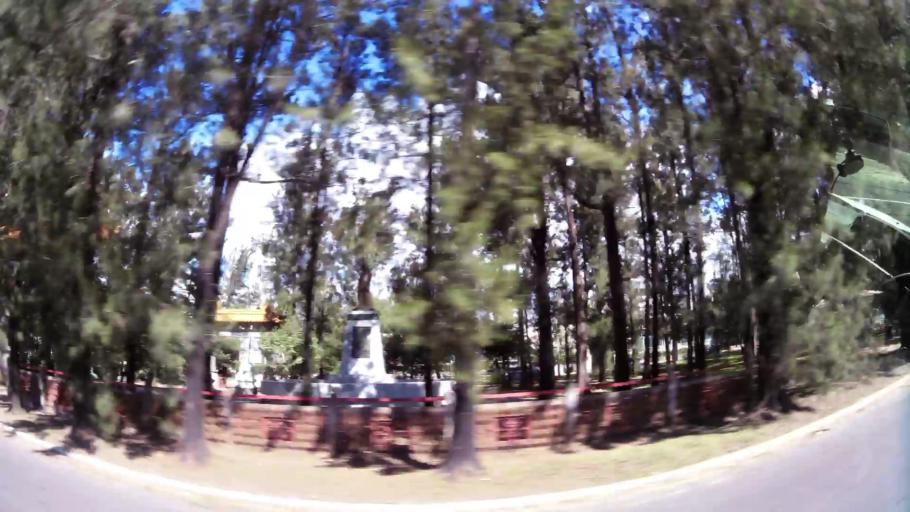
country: GT
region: Guatemala
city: Santa Catarina Pinula
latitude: 14.6033
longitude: -90.5008
